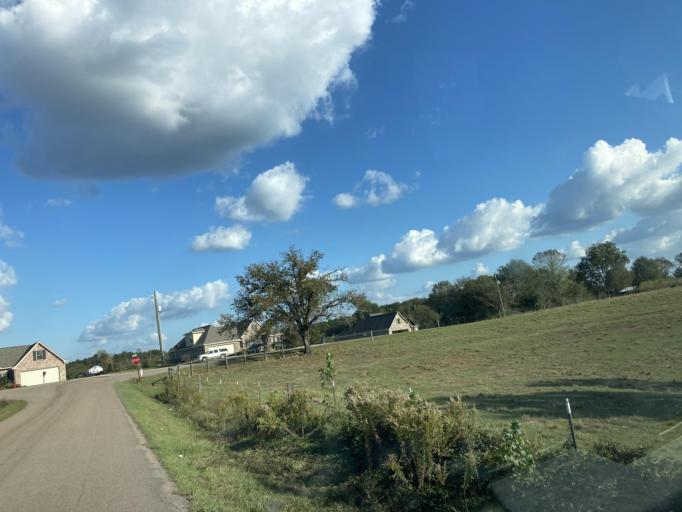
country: US
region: Mississippi
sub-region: Lamar County
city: Sumrall
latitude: 31.4211
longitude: -89.6264
